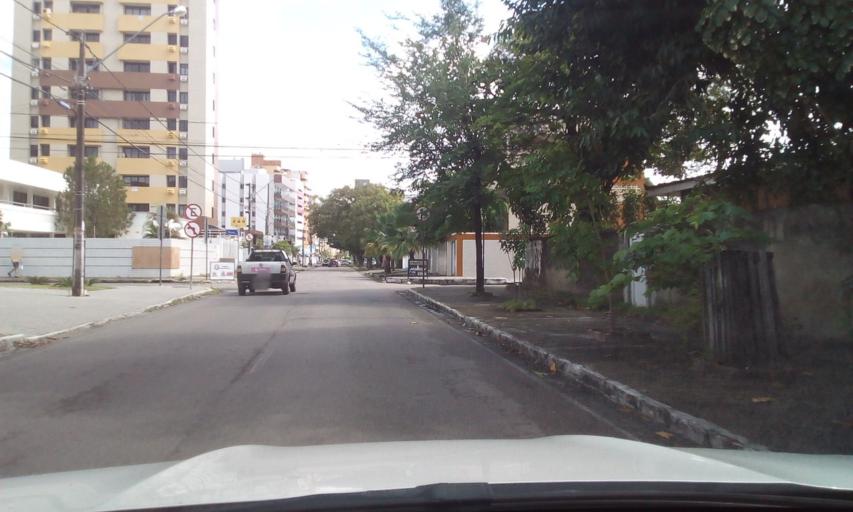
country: BR
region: Paraiba
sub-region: Joao Pessoa
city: Joao Pessoa
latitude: -7.1027
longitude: -34.8334
